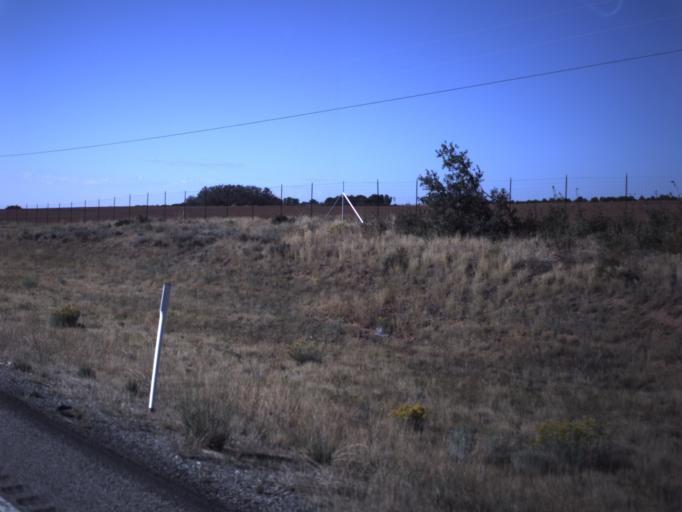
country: US
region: Utah
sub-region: San Juan County
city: Monticello
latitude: 37.8189
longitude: -109.3370
